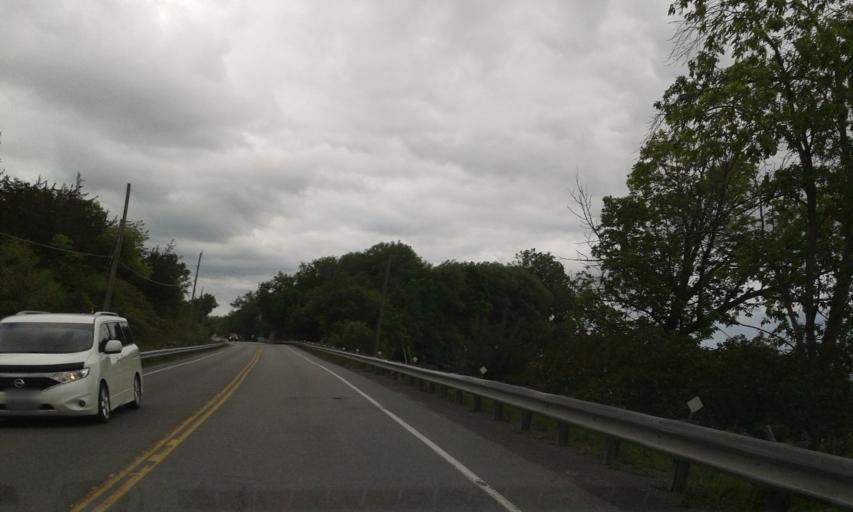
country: CA
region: Ontario
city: Skatepark
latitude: 44.1684
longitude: -76.7924
